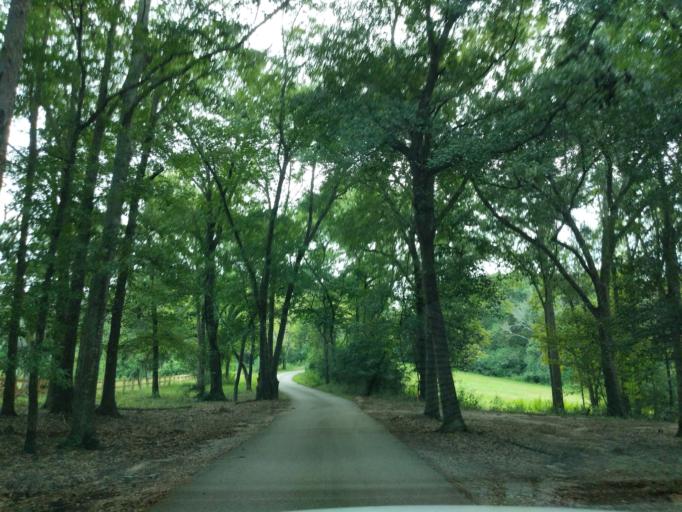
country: US
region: South Carolina
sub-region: Aiken County
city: North Augusta
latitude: 33.5323
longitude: -81.9947
